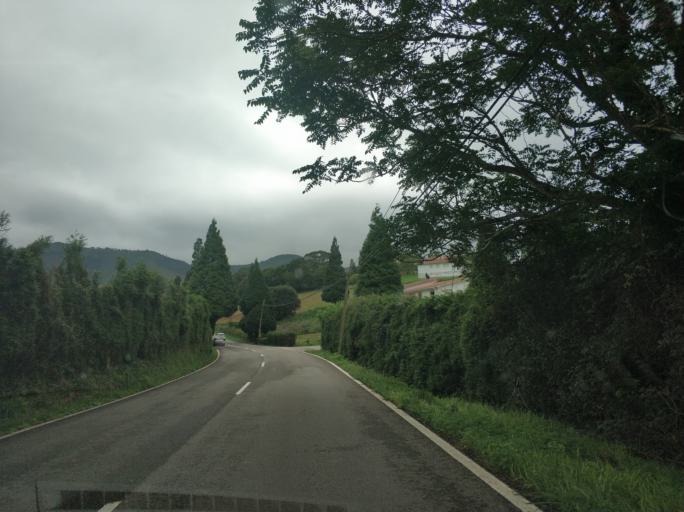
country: ES
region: Asturias
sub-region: Province of Asturias
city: Cudillero
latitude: 43.5513
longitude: -6.2259
